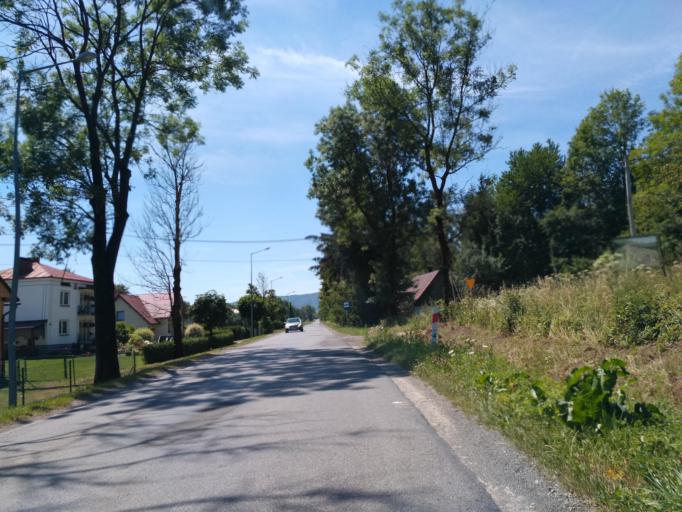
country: PL
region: Subcarpathian Voivodeship
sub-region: Powiat sanocki
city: Bukowsko
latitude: 49.4944
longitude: 22.0694
